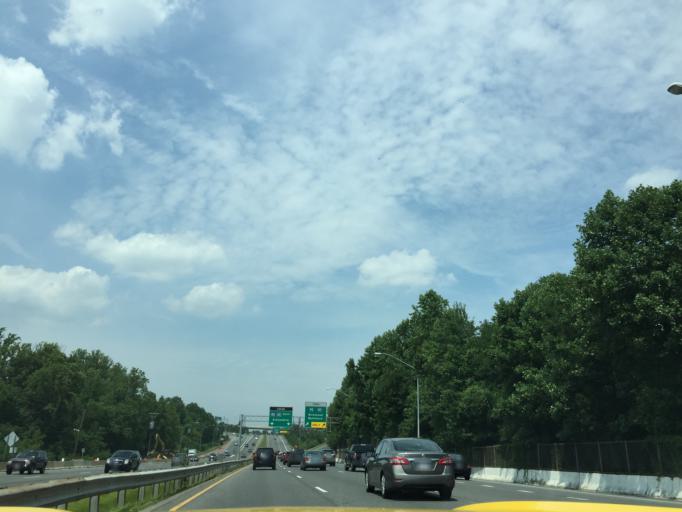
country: US
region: Maryland
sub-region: Prince George's County
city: Oxon Hill
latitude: 38.7924
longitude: -76.9986
